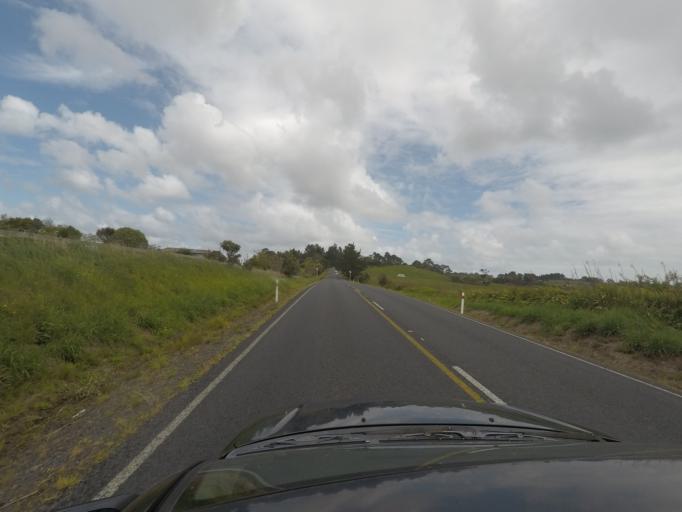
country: NZ
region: Auckland
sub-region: Auckland
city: Parakai
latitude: -36.6344
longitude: 174.5049
